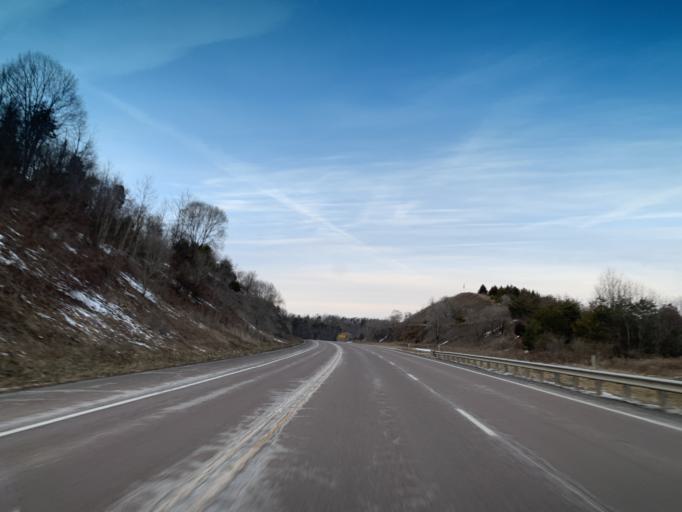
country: US
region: Maryland
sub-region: Allegany County
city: Cumberland
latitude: 39.6870
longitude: -78.7145
